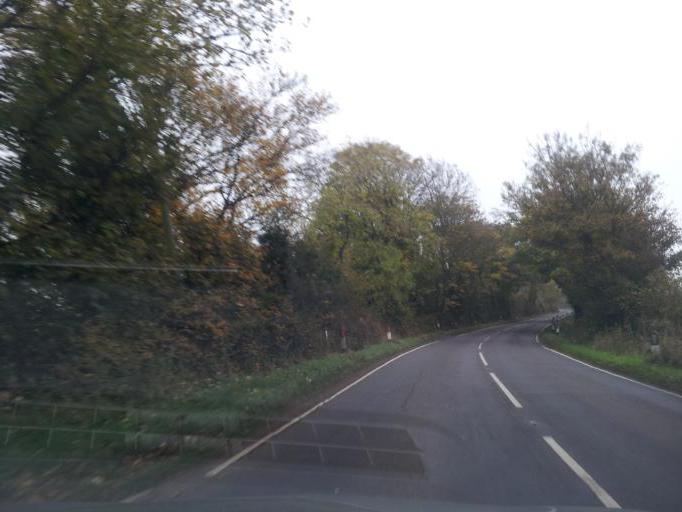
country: GB
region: England
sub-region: Buckinghamshire
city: Buckingham
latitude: 52.0191
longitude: -1.0568
